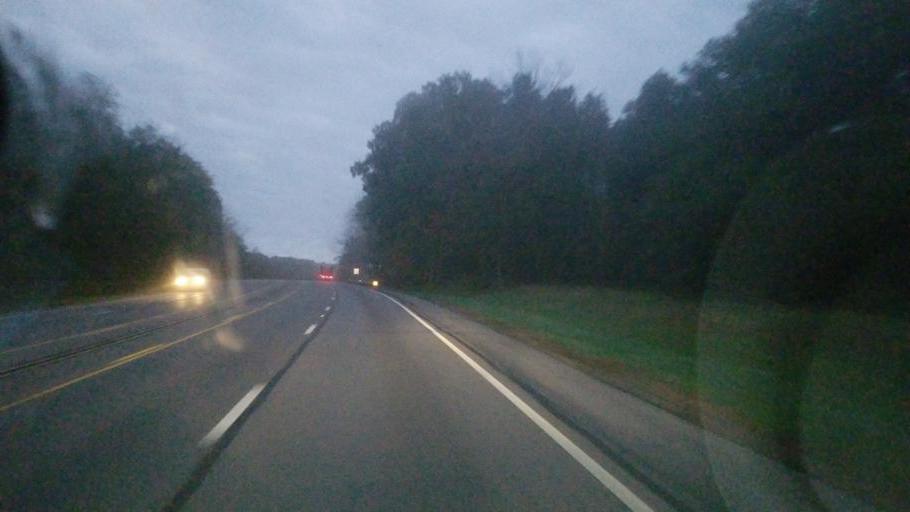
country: US
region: Ohio
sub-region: Pike County
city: Waverly
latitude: 39.2190
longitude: -82.9844
